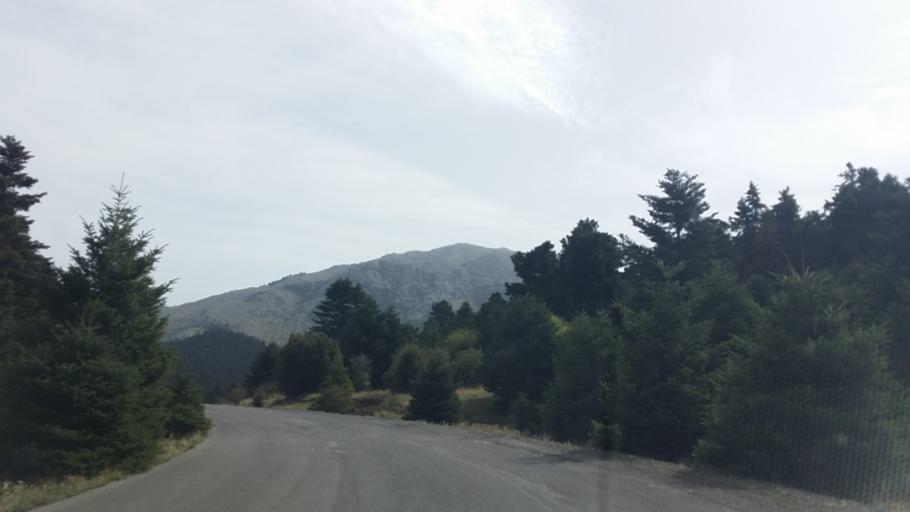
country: GR
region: Central Greece
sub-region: Nomos Voiotias
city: Kyriaki
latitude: 38.3281
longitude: 22.8447
